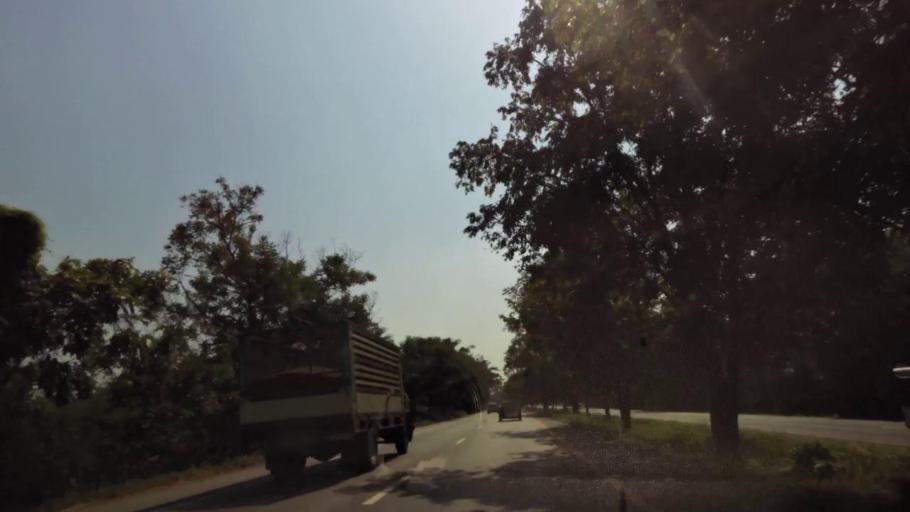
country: TH
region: Phichit
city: Bueng Na Rang
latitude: 16.0227
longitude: 100.1146
